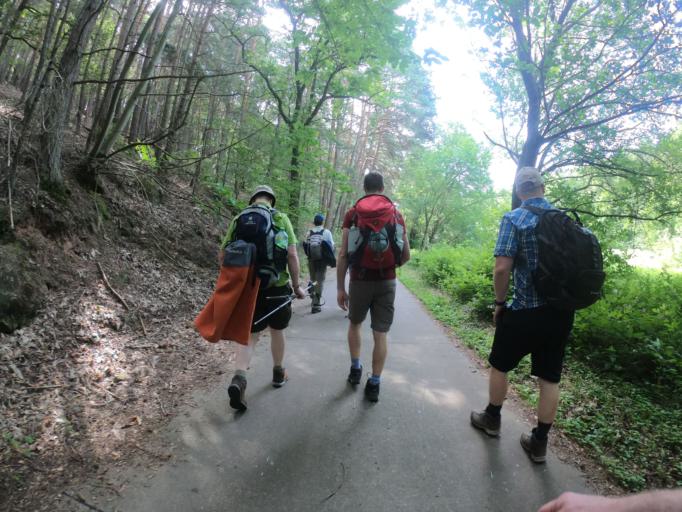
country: DE
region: Rheinland-Pfalz
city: Gleiszellen-Gleishorbach
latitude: 49.1192
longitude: 7.9818
